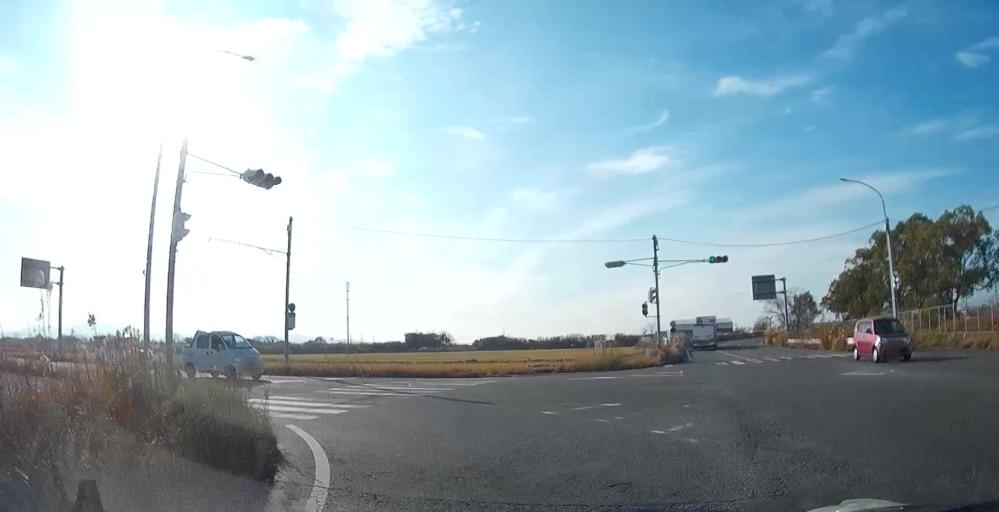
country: JP
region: Kumamoto
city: Uto
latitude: 32.7447
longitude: 130.6763
